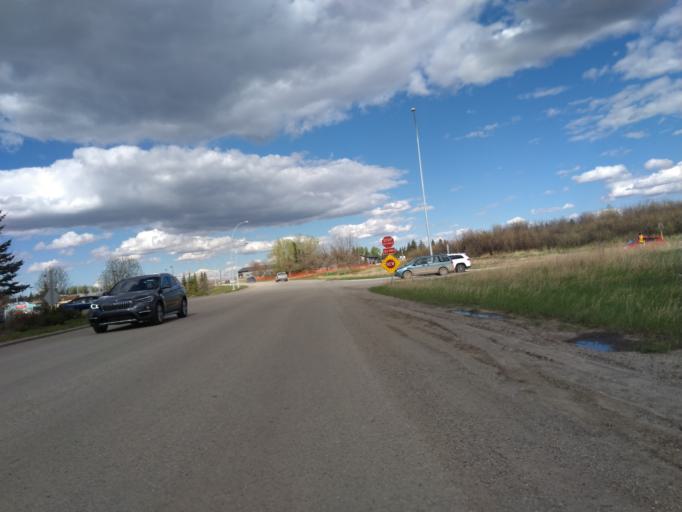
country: CA
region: Alberta
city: Calgary
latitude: 51.0058
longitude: -114.1461
